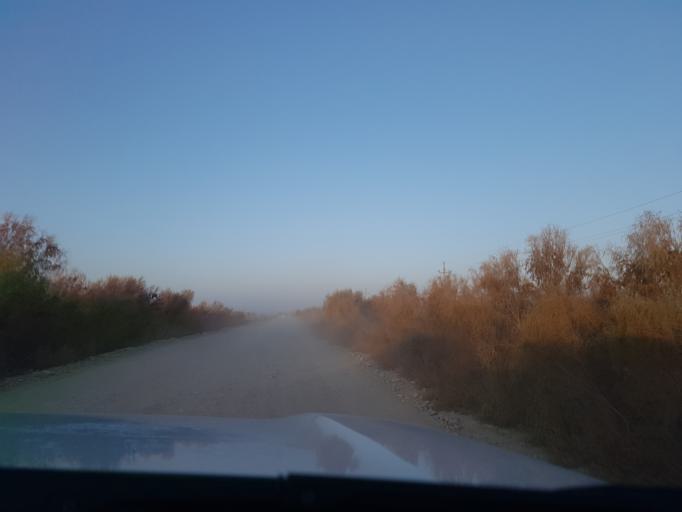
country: TM
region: Dasoguz
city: Koeneuergench
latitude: 41.8447
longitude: 58.5286
